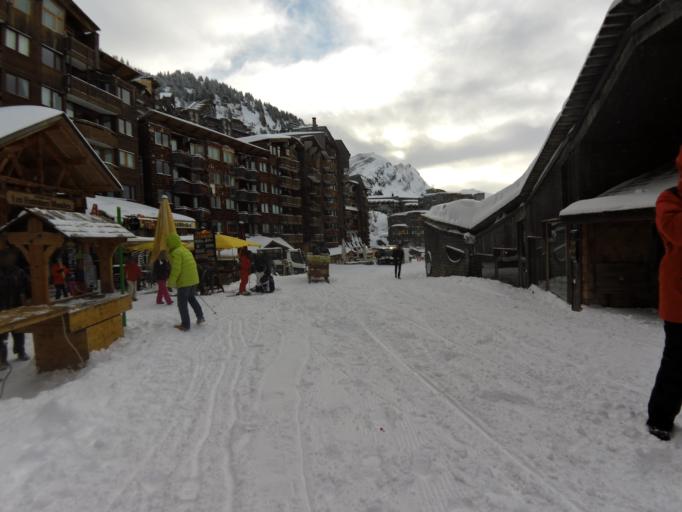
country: FR
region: Rhone-Alpes
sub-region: Departement de la Haute-Savoie
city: Morzine
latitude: 46.1922
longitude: 6.7754
